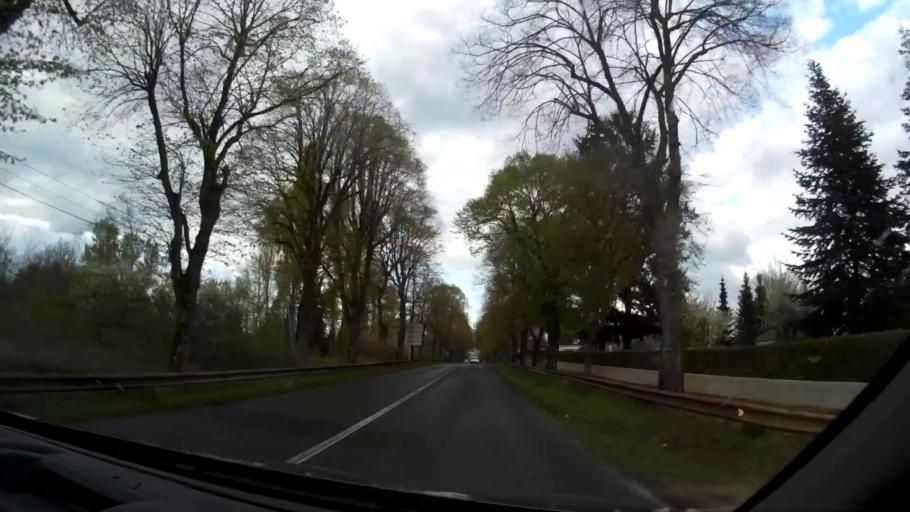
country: FR
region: Centre
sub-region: Departement du Loir-et-Cher
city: Contres
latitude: 47.4303
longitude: 1.4278
